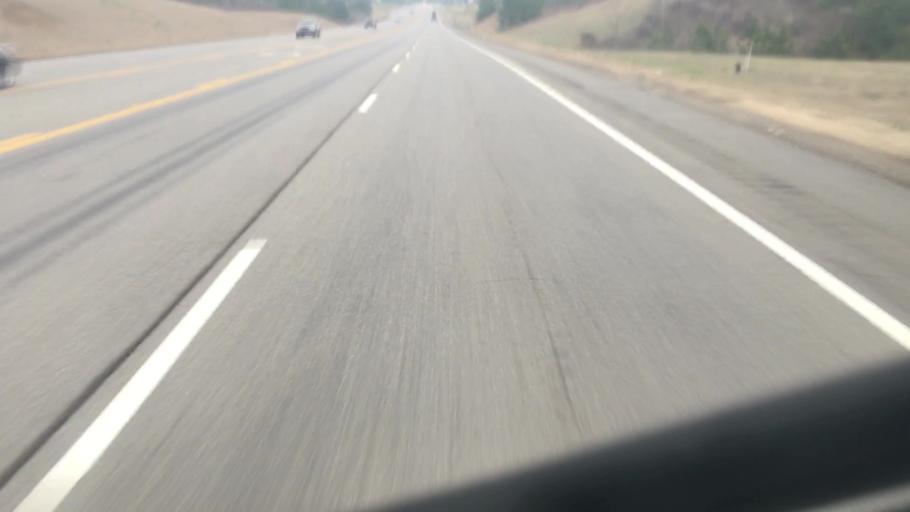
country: US
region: Alabama
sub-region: Walker County
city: Jasper
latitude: 33.8029
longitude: -87.2356
